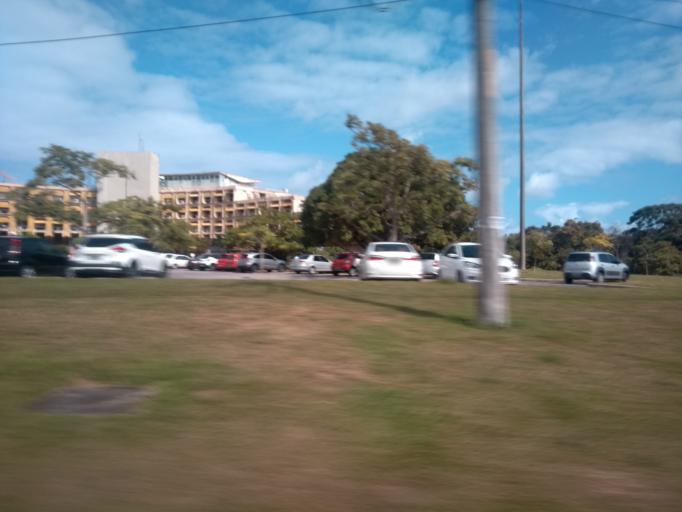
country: BR
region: Bahia
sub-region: Salvador
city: Salvador
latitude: -12.9438
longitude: -38.4292
